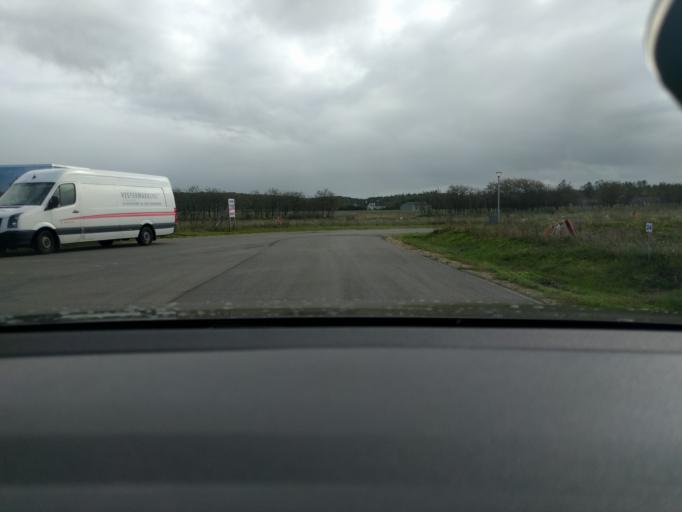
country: DK
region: Central Jutland
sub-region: Viborg Kommune
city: Viborg
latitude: 56.4317
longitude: 9.4232
